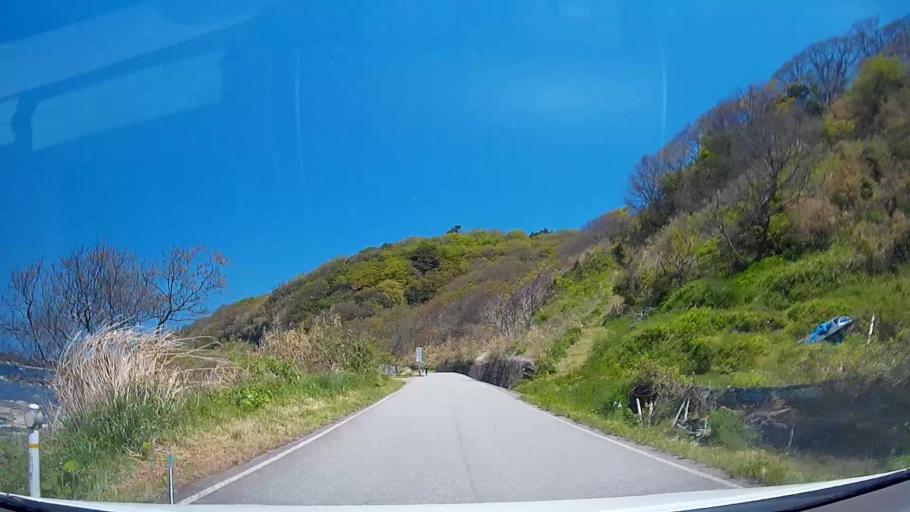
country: JP
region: Ishikawa
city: Nanao
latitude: 37.5213
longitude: 137.2469
